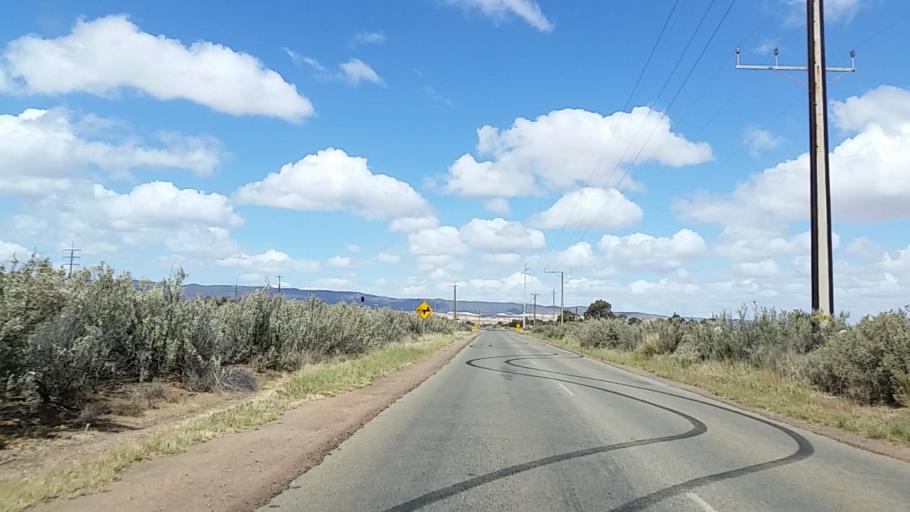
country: AU
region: South Australia
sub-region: Port Pirie City and Dists
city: Solomontown
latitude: -33.1939
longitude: 138.0404
